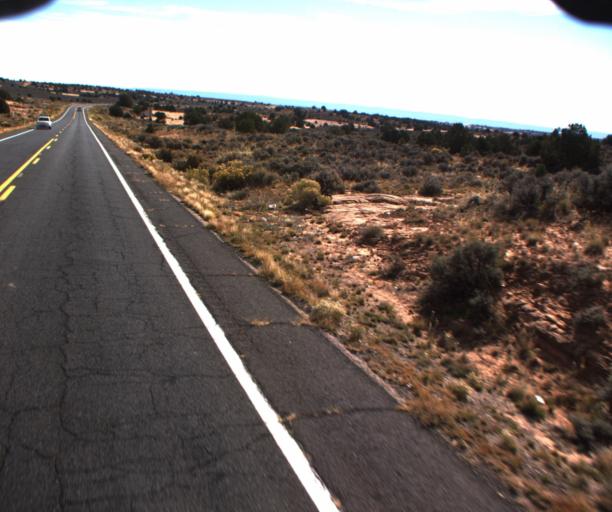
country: US
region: Arizona
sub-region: Coconino County
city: Kaibito
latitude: 36.5777
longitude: -110.7787
